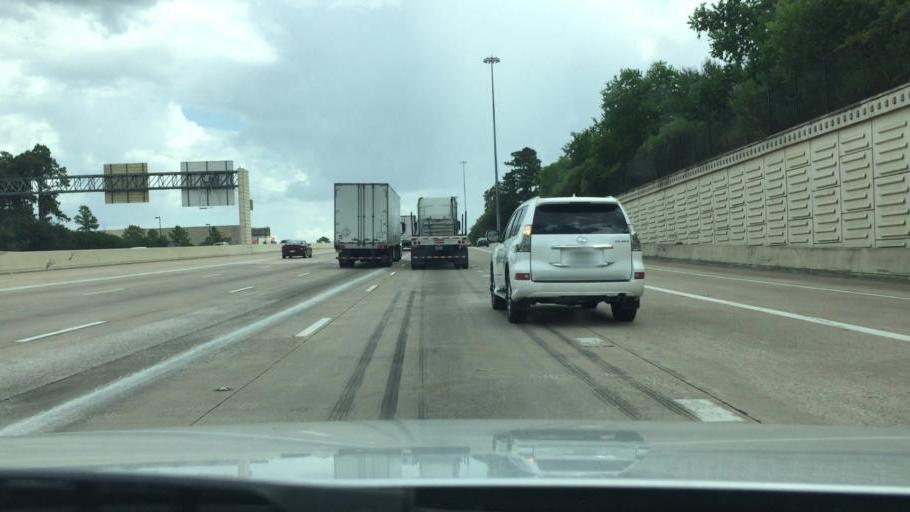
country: US
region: Texas
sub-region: Harris County
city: Hunters Creek Village
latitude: 29.7777
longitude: -95.4428
